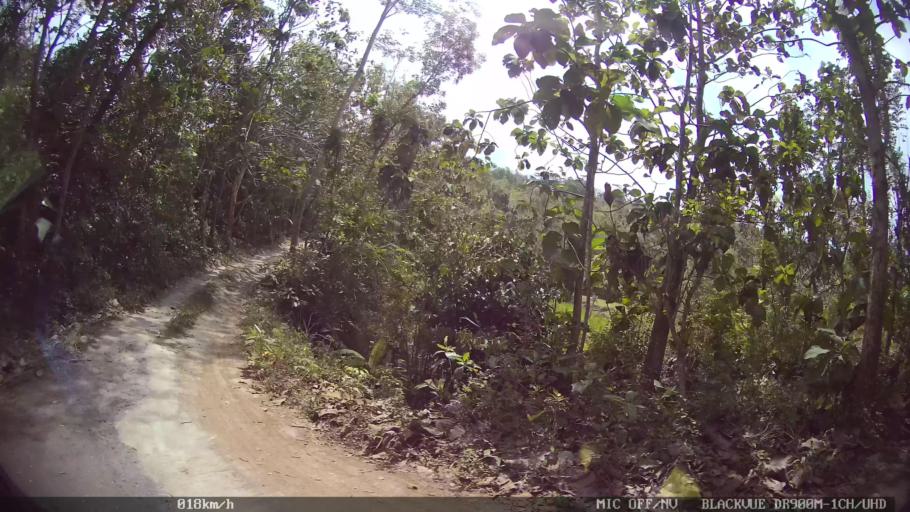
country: ID
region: Central Java
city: Candi Prambanan
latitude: -7.8111
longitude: 110.5234
